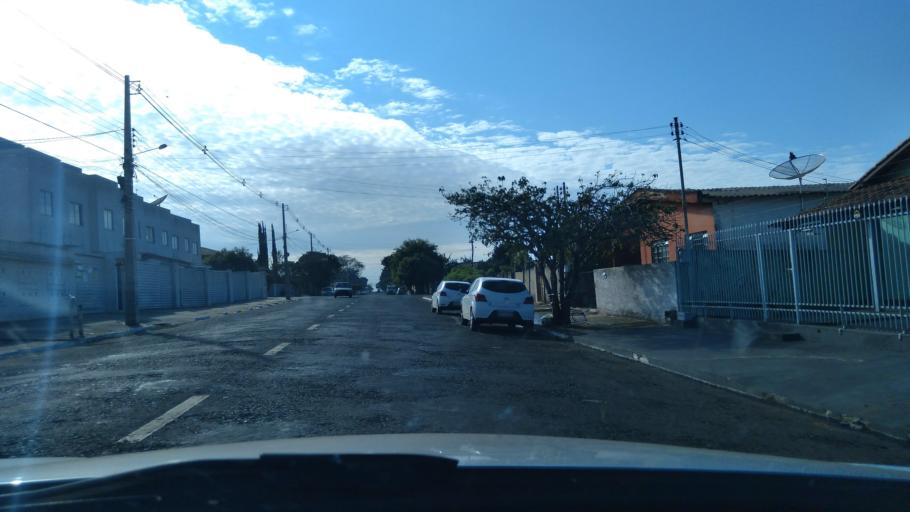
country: BR
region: Goias
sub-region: Mineiros
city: Mineiros
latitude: -17.5586
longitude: -52.5554
